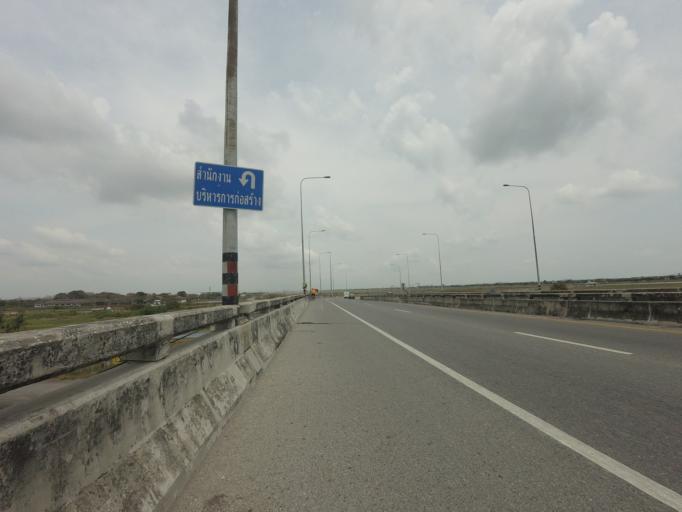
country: TH
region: Bangkok
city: Lat Krabang
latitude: 13.6479
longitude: 100.7462
